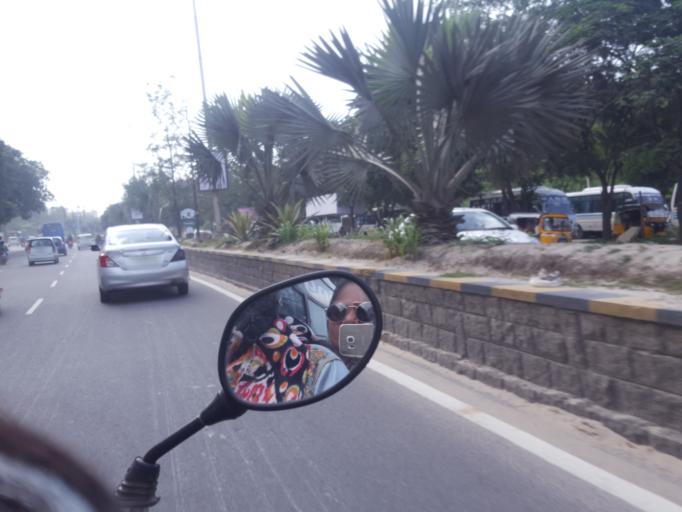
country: IN
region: Telangana
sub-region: Rangareddi
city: Kukatpalli
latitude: 17.4217
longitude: 78.3837
